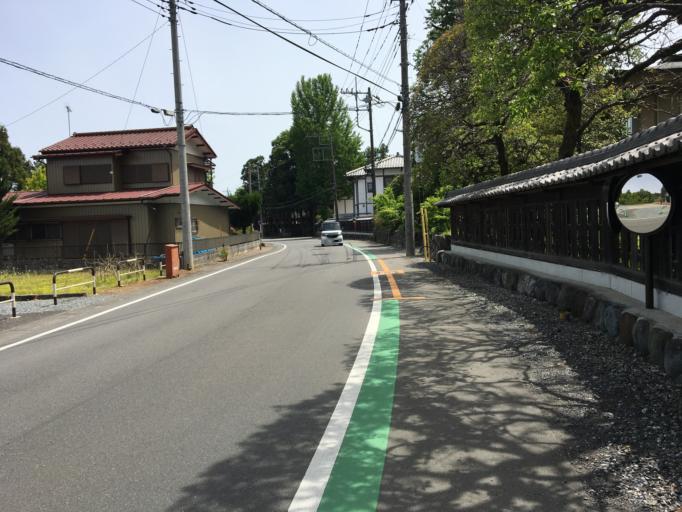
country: JP
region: Saitama
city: Morohongo
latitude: 35.8991
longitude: 139.3228
